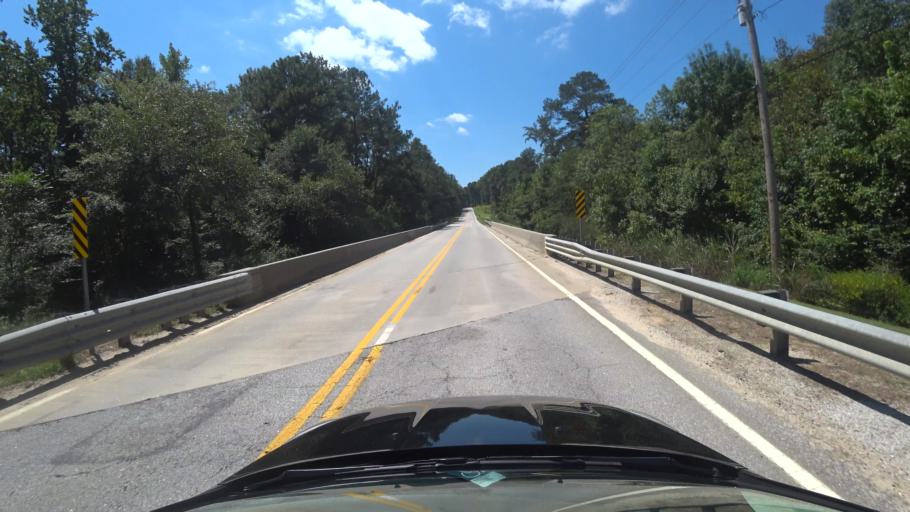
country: US
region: Georgia
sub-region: Newton County
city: Oxford
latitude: 33.6422
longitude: -83.7974
